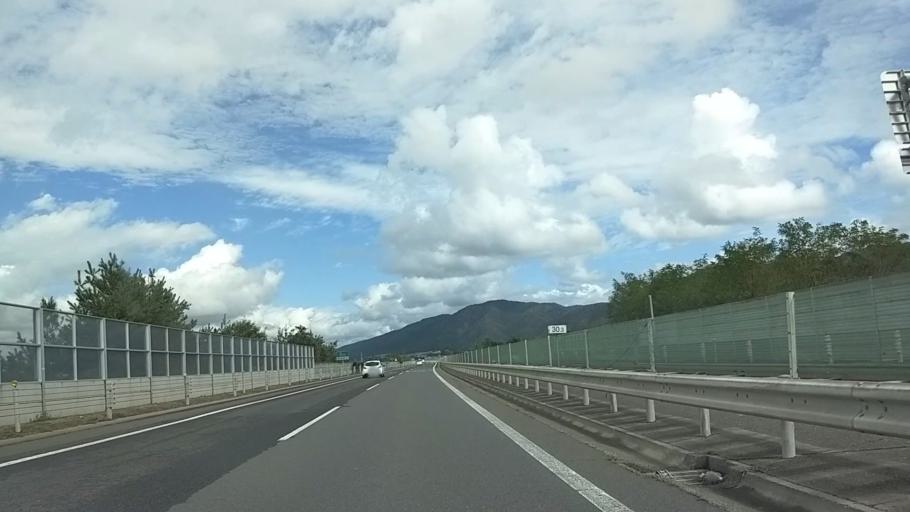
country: JP
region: Nagano
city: Toyoshina
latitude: 36.2736
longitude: 137.9307
